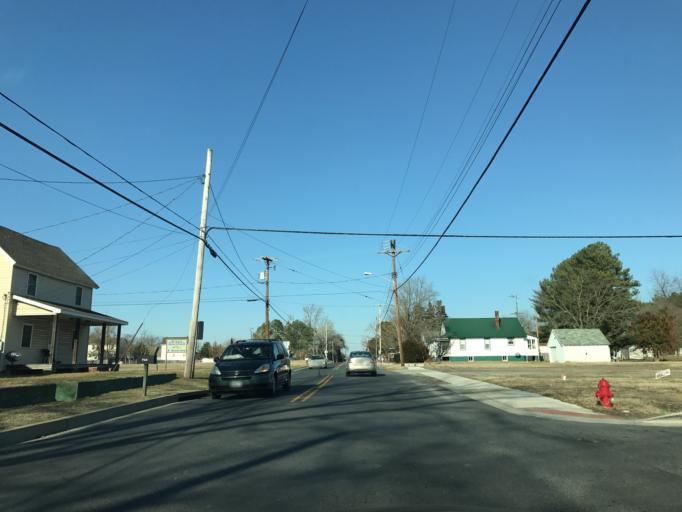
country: US
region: Maryland
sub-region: Caroline County
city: Denton
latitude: 38.8894
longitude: -75.8233
